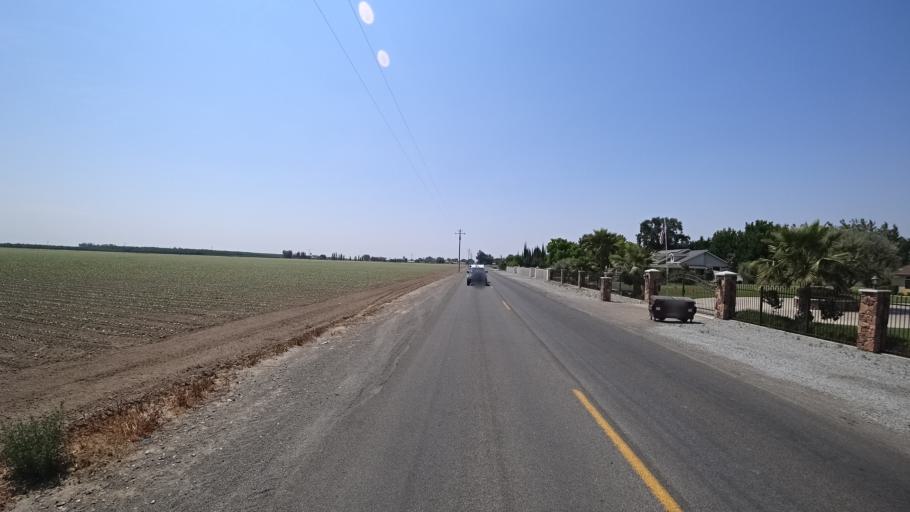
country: US
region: California
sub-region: Kings County
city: Lemoore
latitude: 36.3121
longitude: -119.7629
